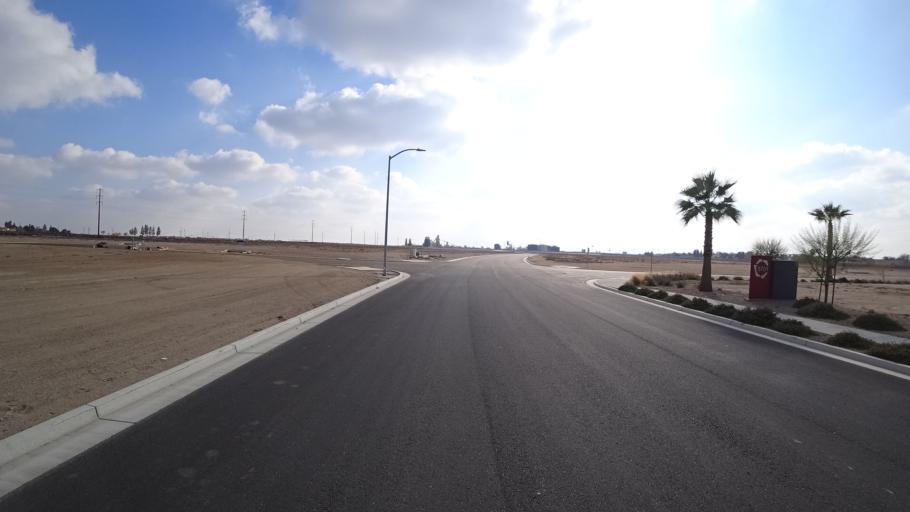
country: US
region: California
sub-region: Kern County
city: Greenacres
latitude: 35.3017
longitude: -119.0985
